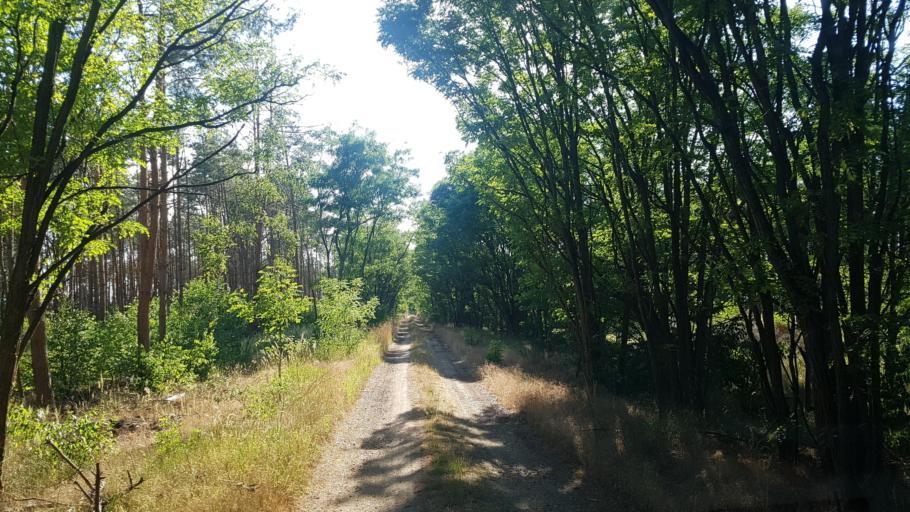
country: DE
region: Brandenburg
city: Muhlberg
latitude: 51.4359
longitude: 13.2962
